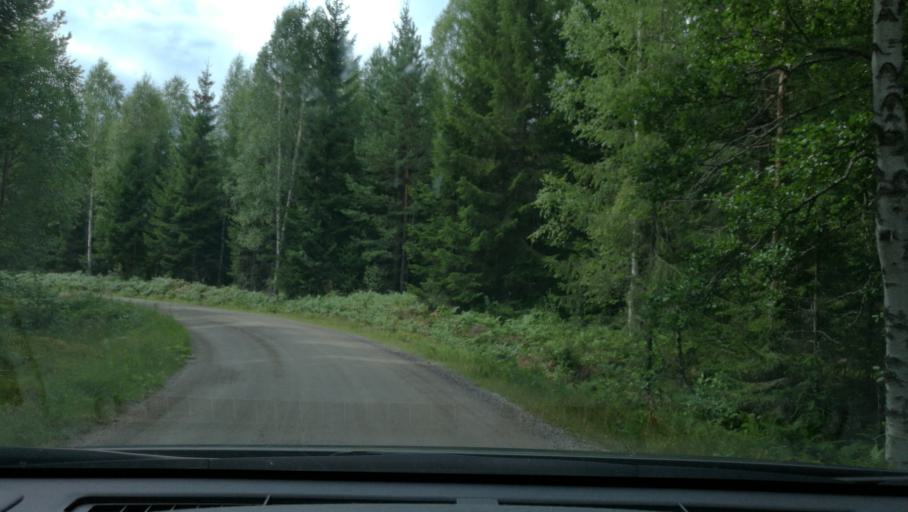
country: SE
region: OEstergoetland
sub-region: Norrkopings Kommun
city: Svartinge
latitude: 58.7564
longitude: 15.9596
